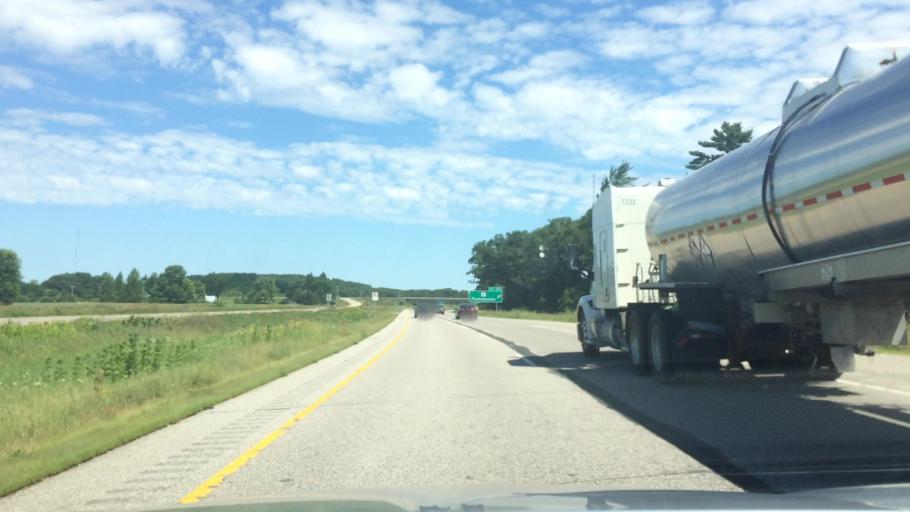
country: US
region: Wisconsin
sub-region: Marquette County
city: Westfield
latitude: 43.7535
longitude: -89.4825
